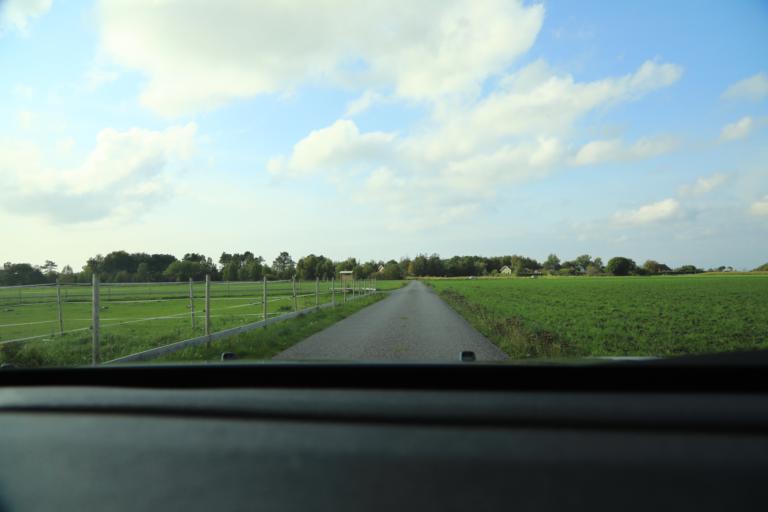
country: SE
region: Halland
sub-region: Varbergs Kommun
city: Tvaaker
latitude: 57.0200
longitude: 12.3461
